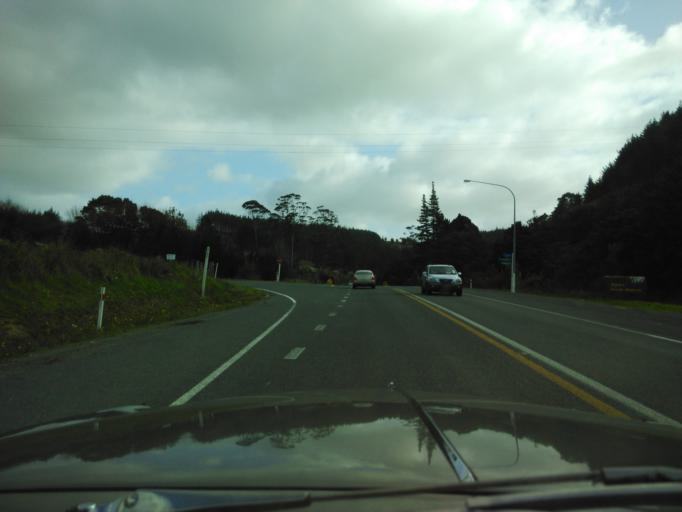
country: NZ
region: Auckland
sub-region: Auckland
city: Wellsford
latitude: -36.2125
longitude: 174.4688
